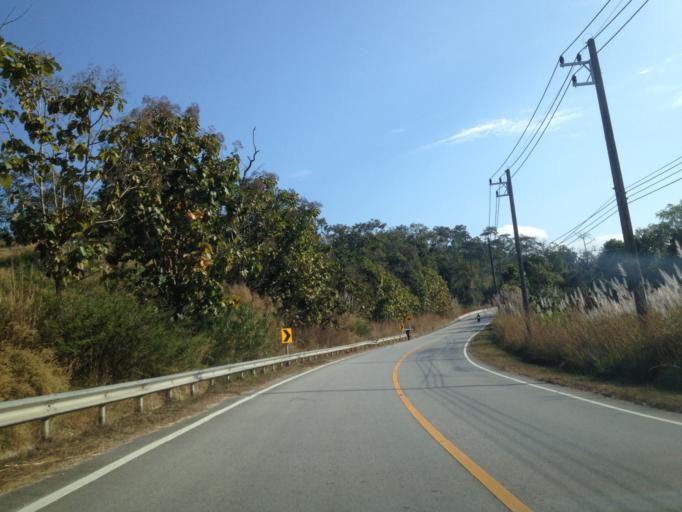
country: TH
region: Mae Hong Son
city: Pa Pae
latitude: 18.1665
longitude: 98.2252
